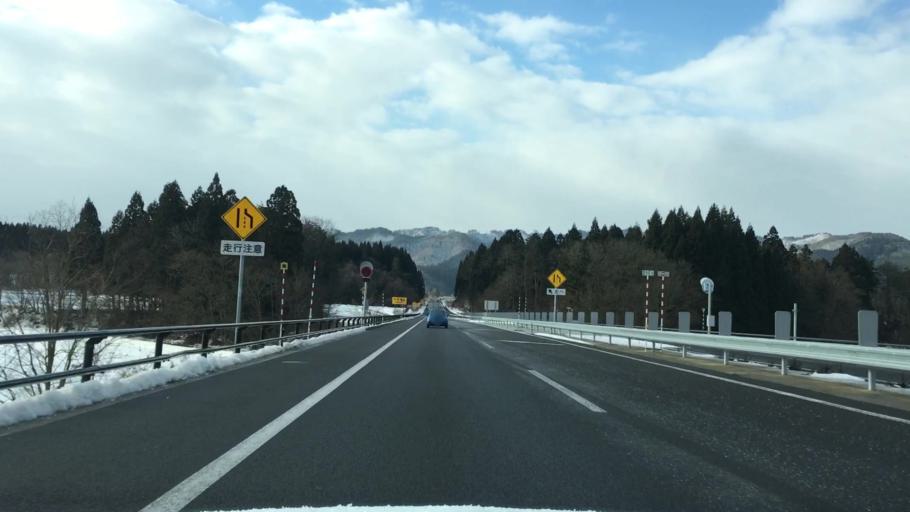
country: JP
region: Akita
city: Odate
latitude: 40.2462
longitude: 140.5118
